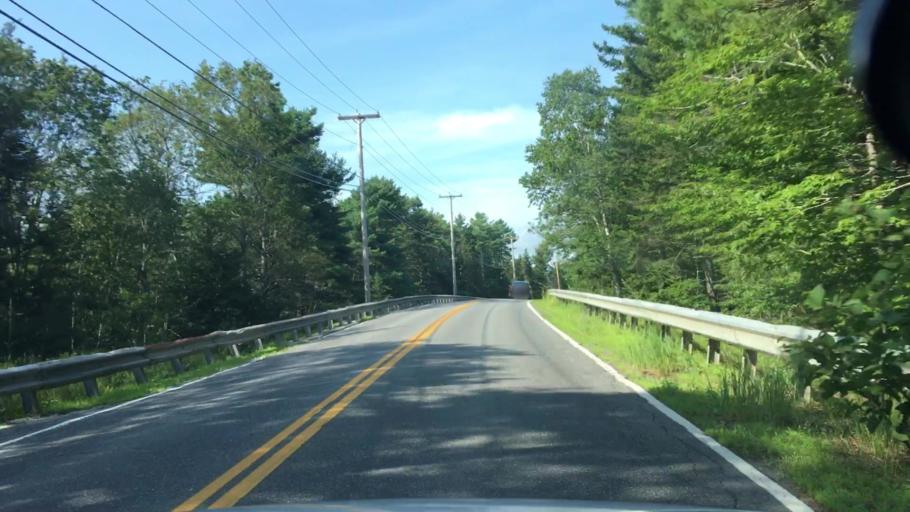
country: US
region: Maine
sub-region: Cumberland County
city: Harpswell Center
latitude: 43.7879
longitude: -69.9491
